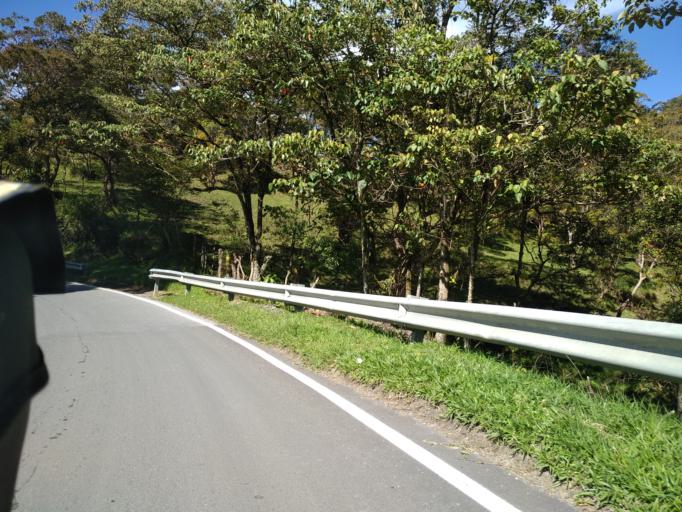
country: CO
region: Santander
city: Velez
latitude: 6.0020
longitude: -73.6833
